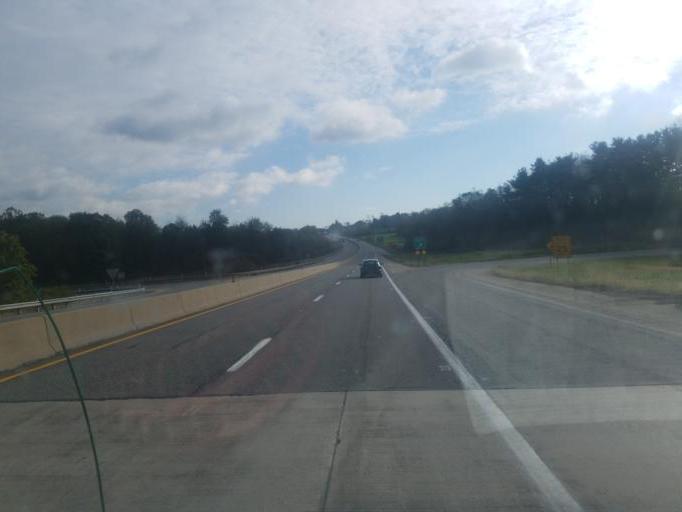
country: US
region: Pennsylvania
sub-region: Indiana County
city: Homer City
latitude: 40.4559
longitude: -79.0320
